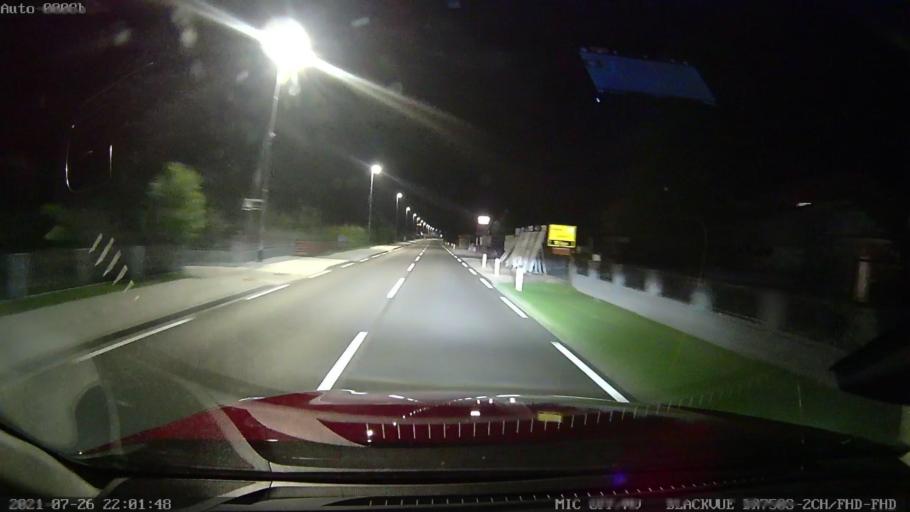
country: SI
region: Markovci
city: Markovci
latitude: 46.3860
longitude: 15.9625
